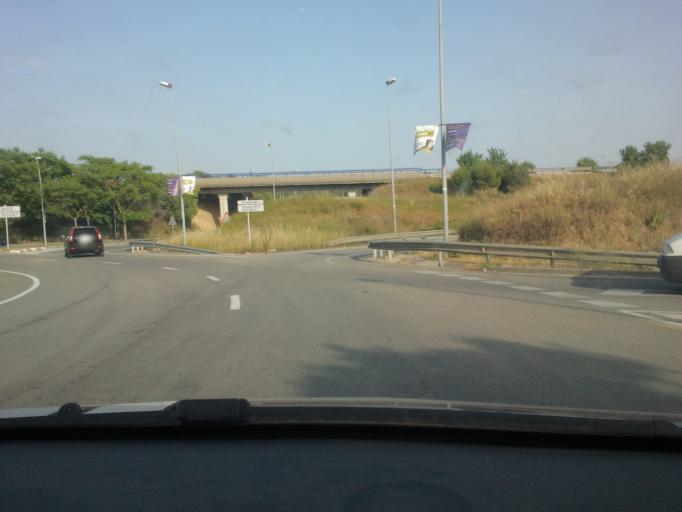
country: ES
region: Catalonia
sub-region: Provincia de Barcelona
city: Vilafranca del Penedes
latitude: 41.3368
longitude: 1.7053
